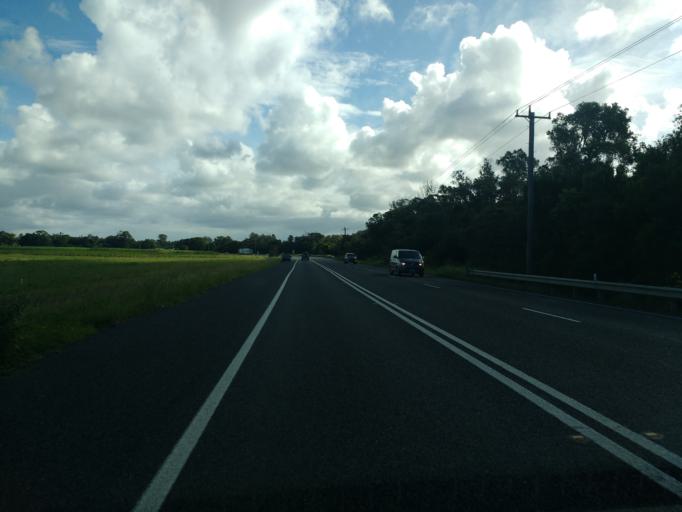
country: AU
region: New South Wales
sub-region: Richmond Valley
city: Evans Head
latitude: -28.9990
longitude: 153.4439
